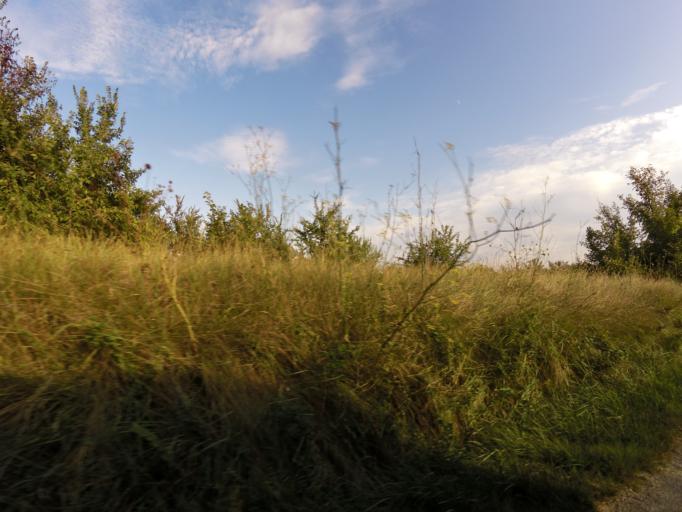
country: FR
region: Languedoc-Roussillon
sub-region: Departement du Gard
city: Gallargues-le-Montueux
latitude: 43.7107
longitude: 4.1709
